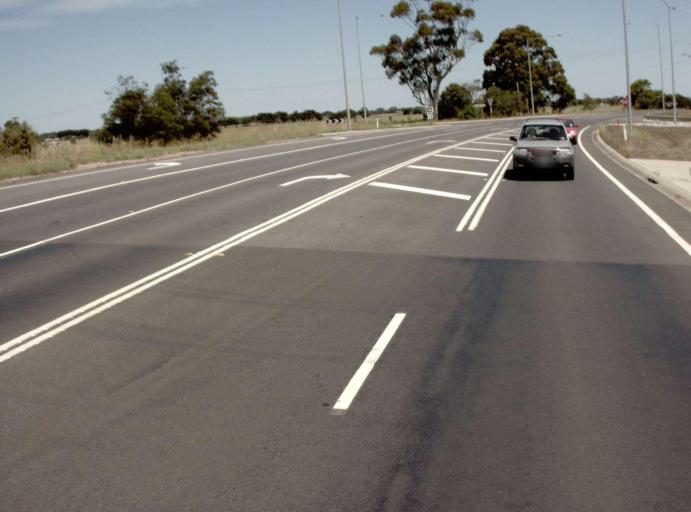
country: AU
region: Victoria
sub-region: Wellington
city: Sale
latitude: -38.0670
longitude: 147.0734
